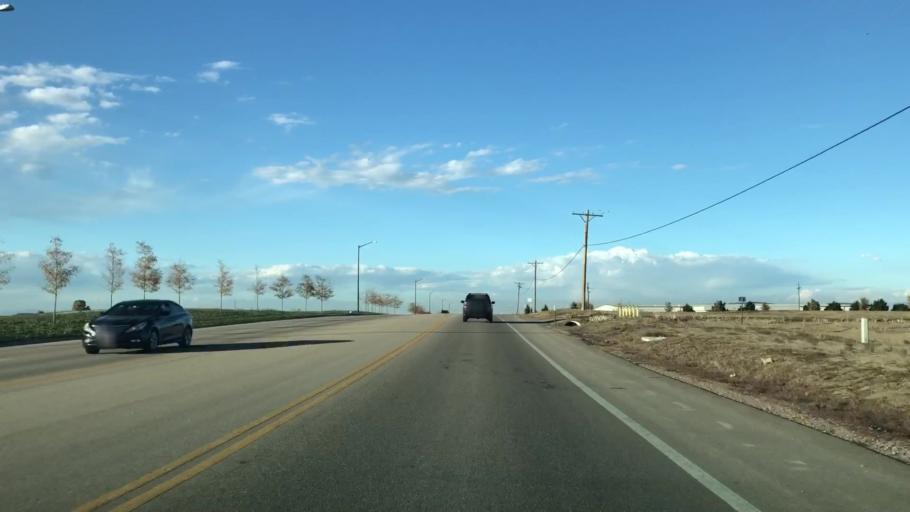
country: US
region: Colorado
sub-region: Larimer County
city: Loveland
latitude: 40.4377
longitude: -105.0204
